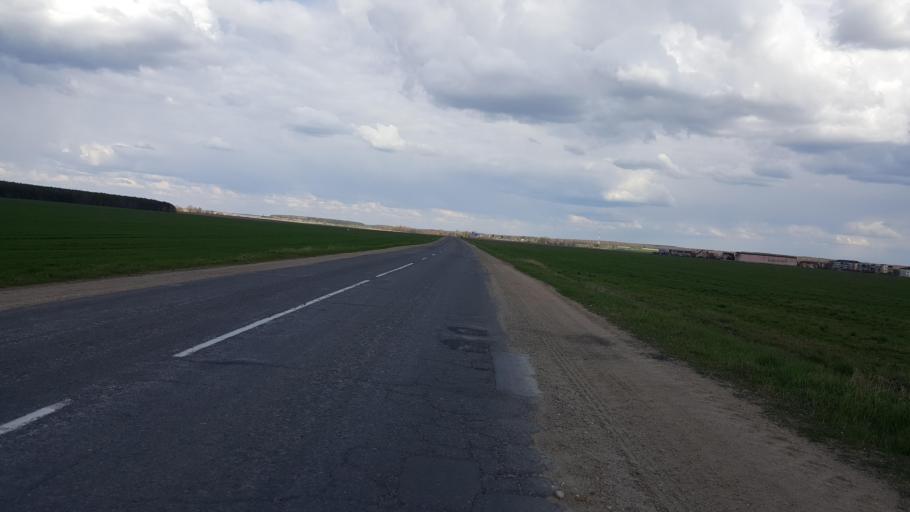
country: BY
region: Brest
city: Kamyanyets
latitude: 52.4161
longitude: 23.6265
